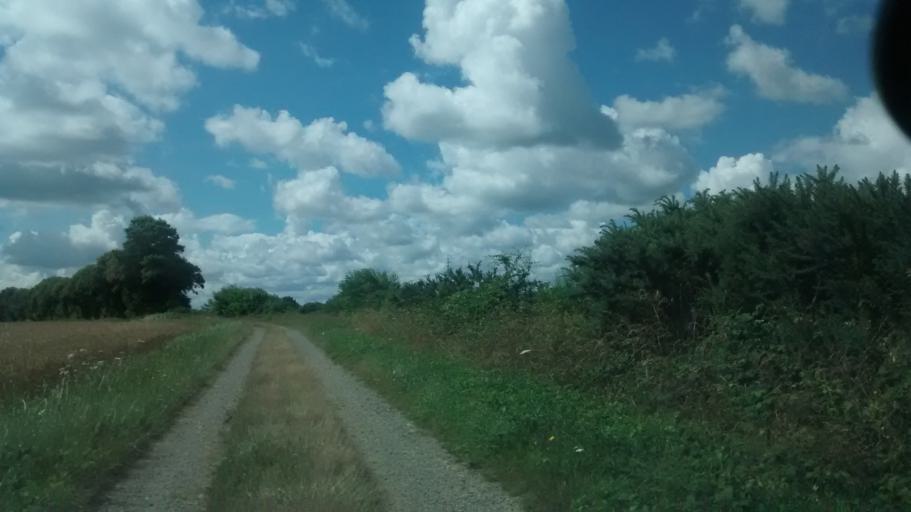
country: FR
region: Brittany
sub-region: Departement d'Ille-et-Vilaine
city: Grand-Fougeray
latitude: 47.7741
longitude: -1.7542
